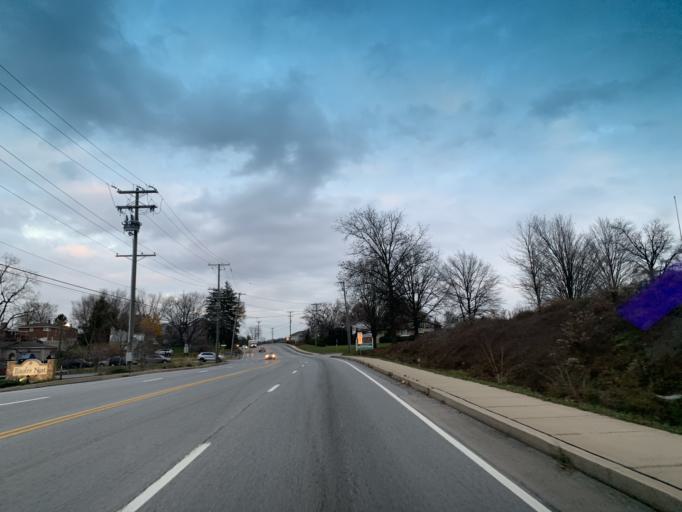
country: US
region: Pennsylvania
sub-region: York County
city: East York
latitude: 39.9587
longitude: -76.6733
